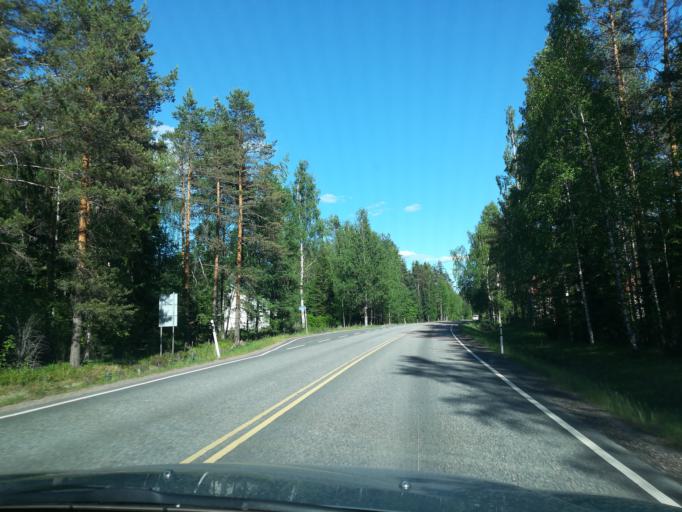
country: FI
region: South Karelia
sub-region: Imatra
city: Ruokolahti
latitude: 61.3995
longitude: 28.6243
